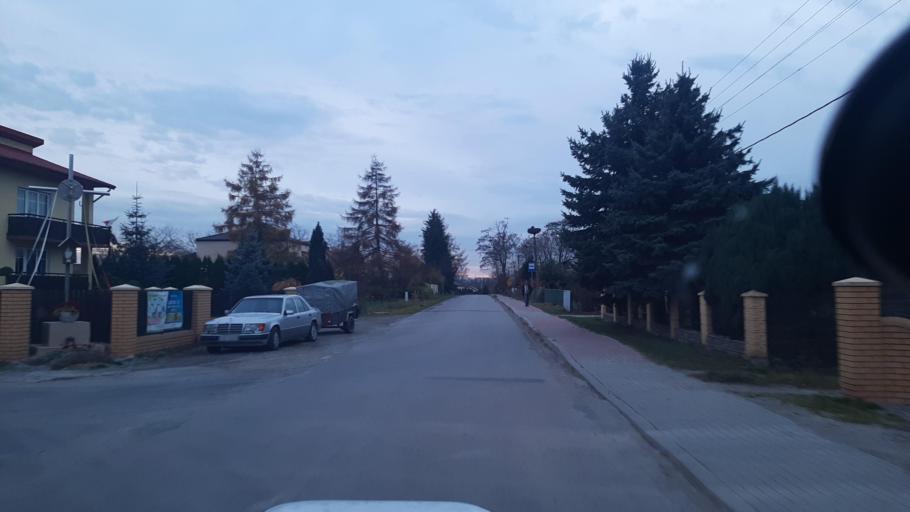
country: PL
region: Lublin Voivodeship
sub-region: Powiat lubelski
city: Garbow
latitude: 51.3594
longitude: 22.3750
